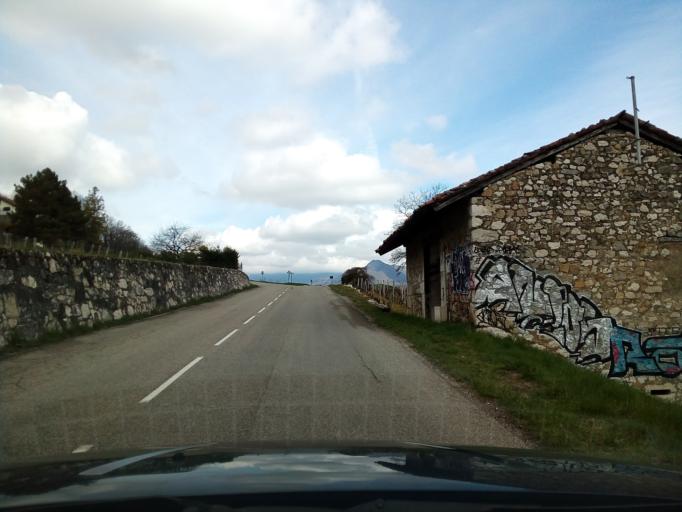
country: FR
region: Rhone-Alpes
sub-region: Departement de la Savoie
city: Les Marches
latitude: 45.4919
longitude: 5.9837
